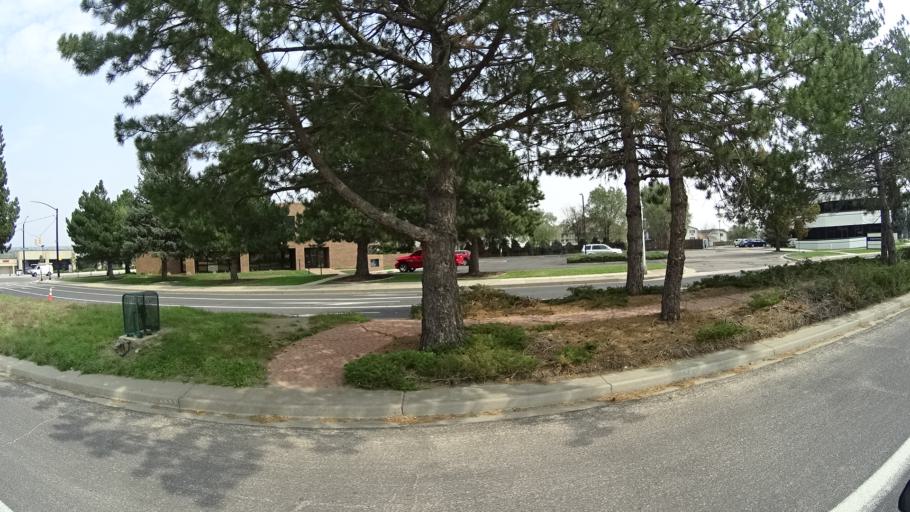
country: US
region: Colorado
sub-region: El Paso County
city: Colorado Springs
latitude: 38.8319
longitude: -104.7884
